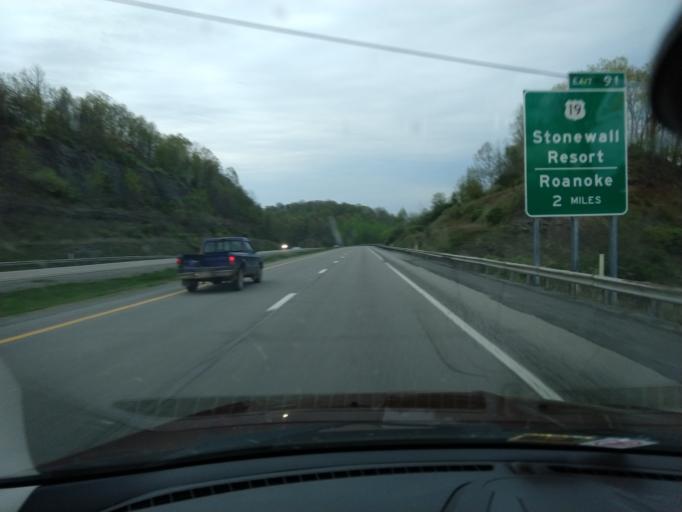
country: US
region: West Virginia
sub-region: Lewis County
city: Weston
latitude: 38.9450
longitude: -80.5384
